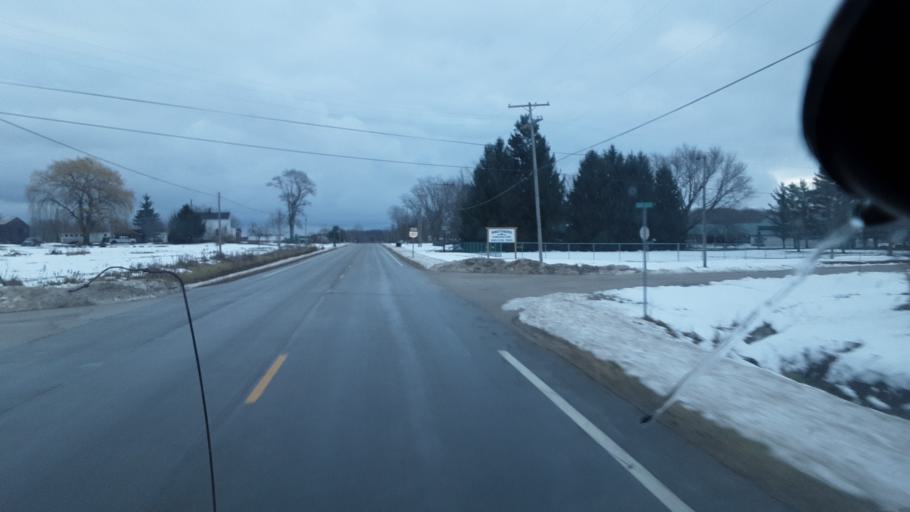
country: US
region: Ohio
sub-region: Ashtabula County
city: Jefferson
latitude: 41.7187
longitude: -80.7420
